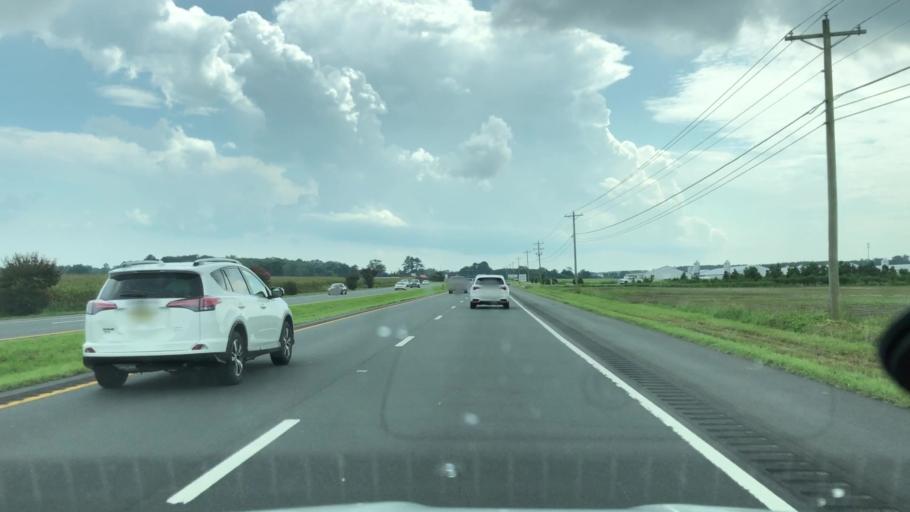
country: US
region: Virginia
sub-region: Accomack County
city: Accomac
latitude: 37.7848
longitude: -75.6077
